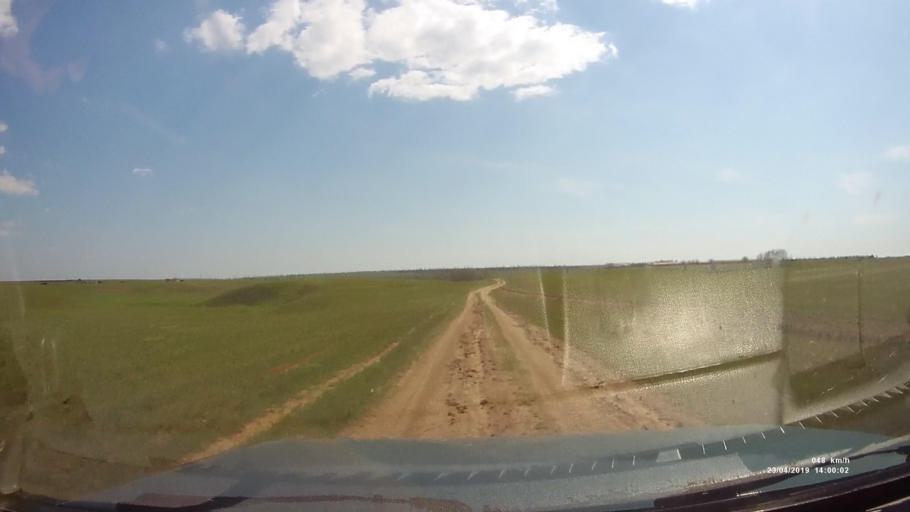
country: RU
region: Rostov
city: Remontnoye
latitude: 46.5623
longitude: 42.9469
